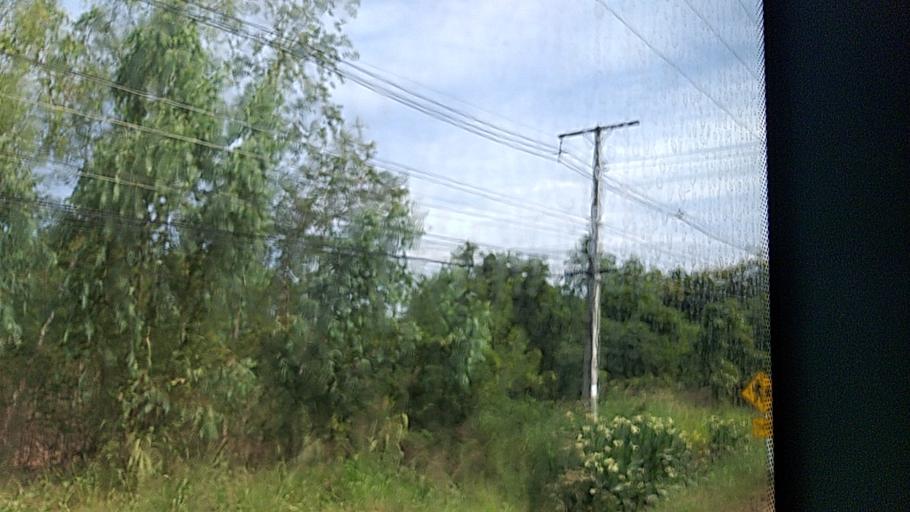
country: TH
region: Maha Sarakham
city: Chiang Yuen
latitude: 16.4431
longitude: 102.9931
